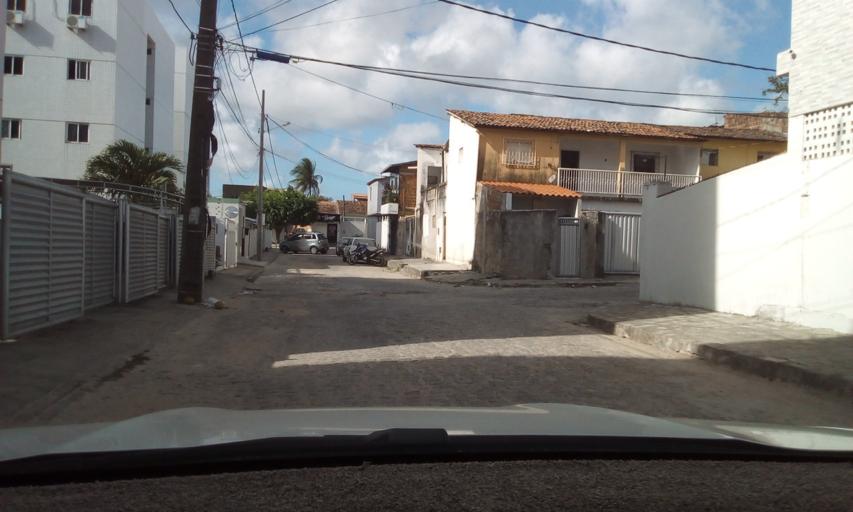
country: BR
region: Paraiba
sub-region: Joao Pessoa
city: Joao Pessoa
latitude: -7.1709
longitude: -34.8442
